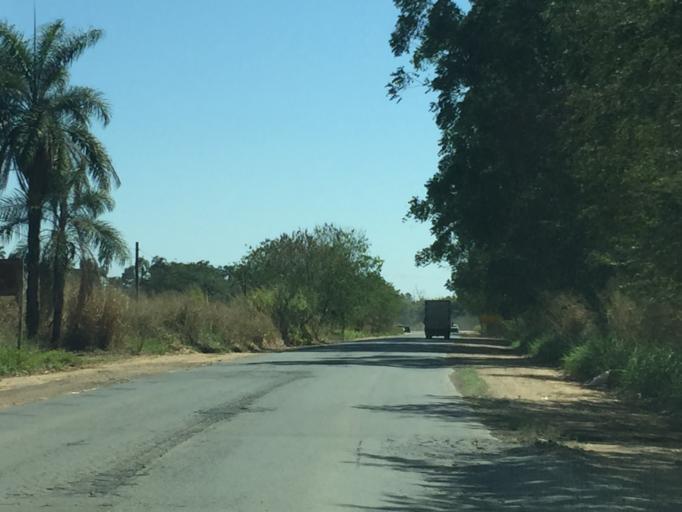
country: BR
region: Sao Paulo
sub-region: Itapira
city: Itapira
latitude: -22.4034
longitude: -46.8457
